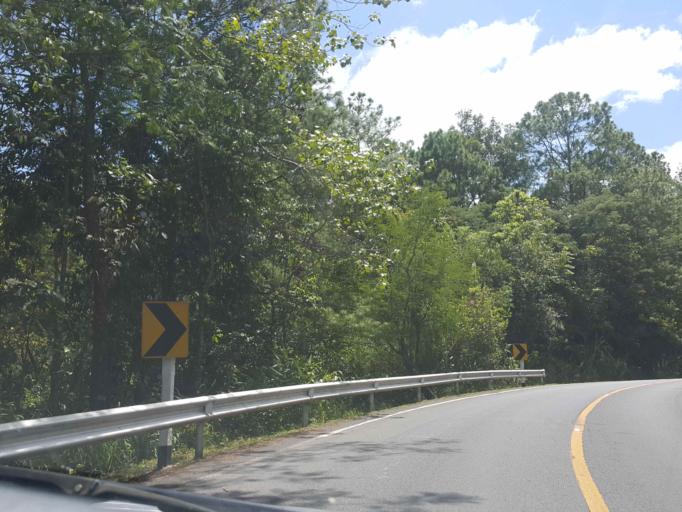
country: TH
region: Chiang Mai
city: Chom Thong
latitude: 18.5420
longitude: 98.5781
